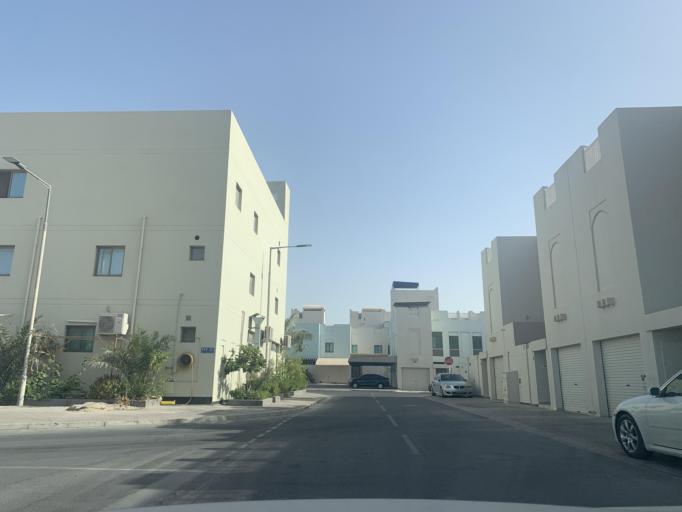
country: BH
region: Northern
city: Sitrah
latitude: 26.1608
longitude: 50.6269
